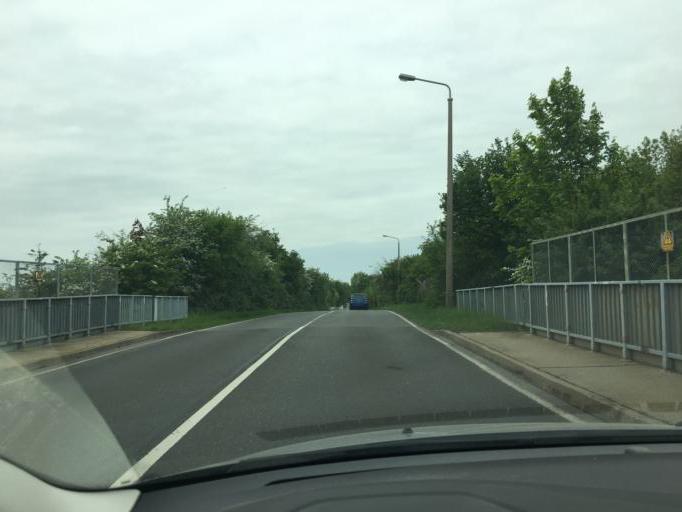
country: DE
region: Saxony
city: Taucha
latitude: 51.3648
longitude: 12.4490
